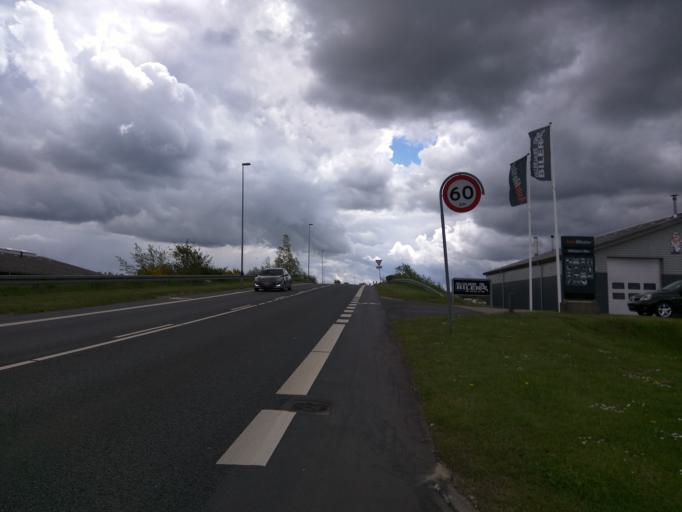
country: DK
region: Central Jutland
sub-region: Viborg Kommune
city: Viborg
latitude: 56.4565
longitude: 9.3687
